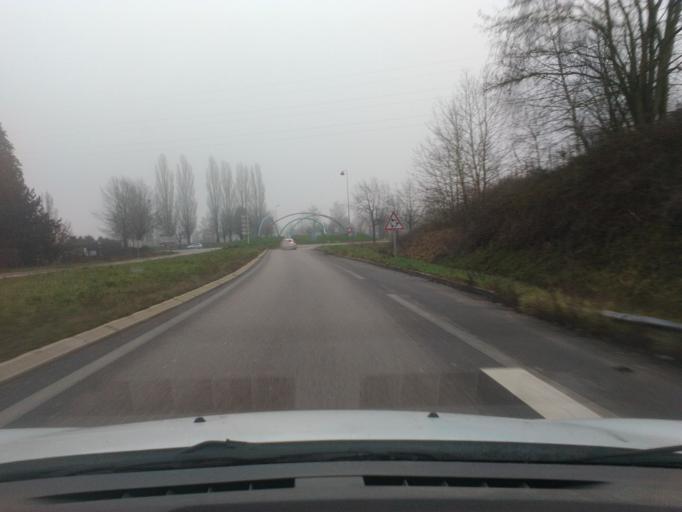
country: FR
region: Lorraine
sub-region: Departement des Vosges
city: Chavelot
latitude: 48.2229
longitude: 6.4338
